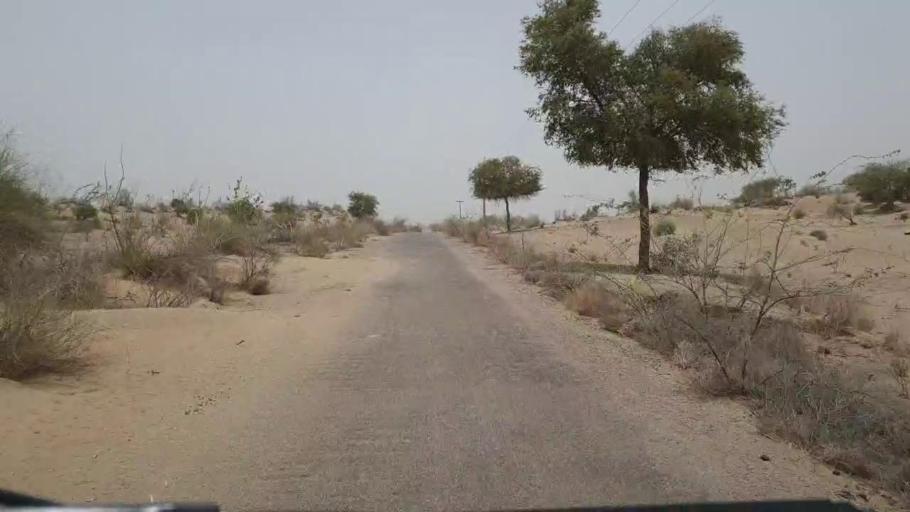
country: PK
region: Sindh
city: Naukot
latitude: 24.7501
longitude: 69.5513
